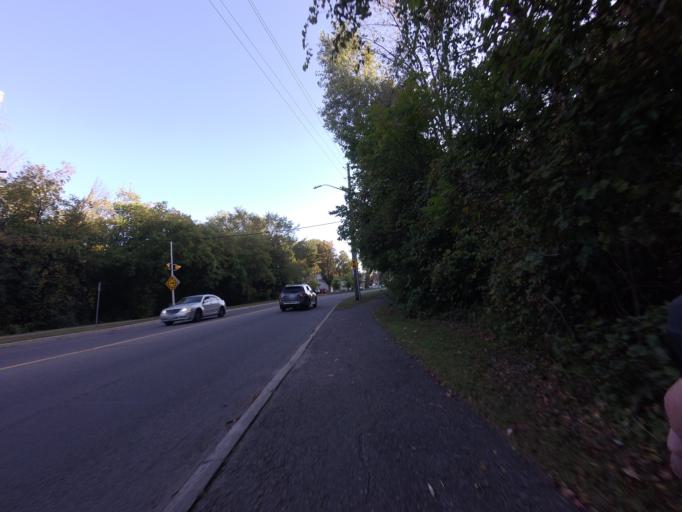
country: CA
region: Ontario
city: Ottawa
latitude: 45.3564
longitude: -75.6726
